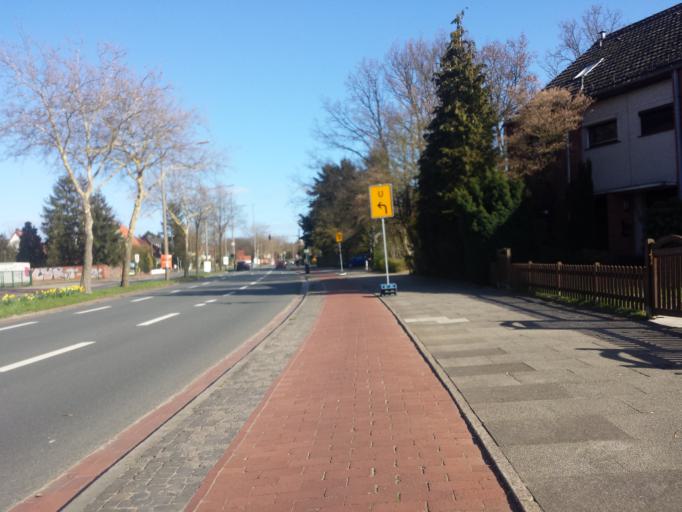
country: DE
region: Lower Saxony
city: Lilienthal
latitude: 53.0697
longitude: 8.9323
